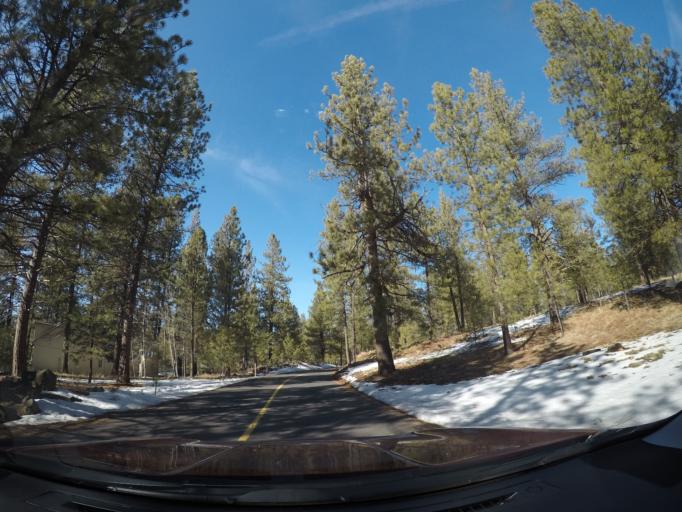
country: US
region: Oregon
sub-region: Deschutes County
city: Sunriver
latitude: 43.8736
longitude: -121.4313
